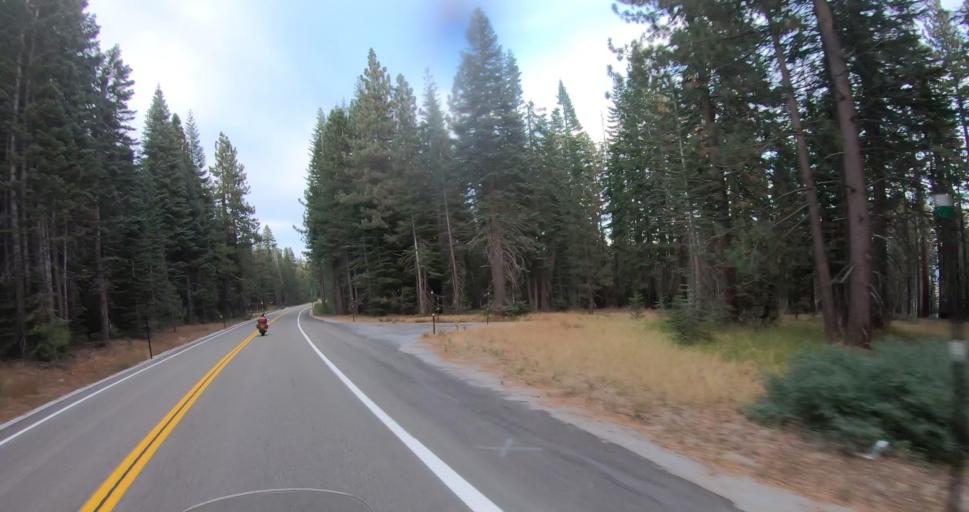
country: US
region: California
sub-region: Calaveras County
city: Arnold
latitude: 38.4010
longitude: -120.1636
